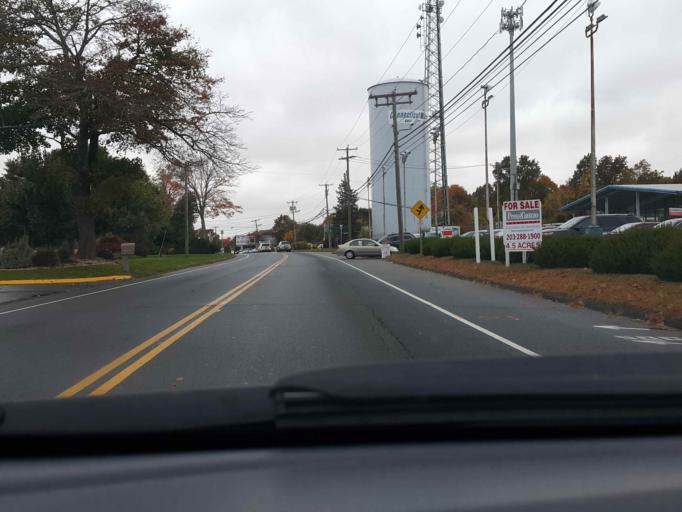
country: US
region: Connecticut
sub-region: New Haven County
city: Guilford Center
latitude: 41.2878
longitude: -72.6570
